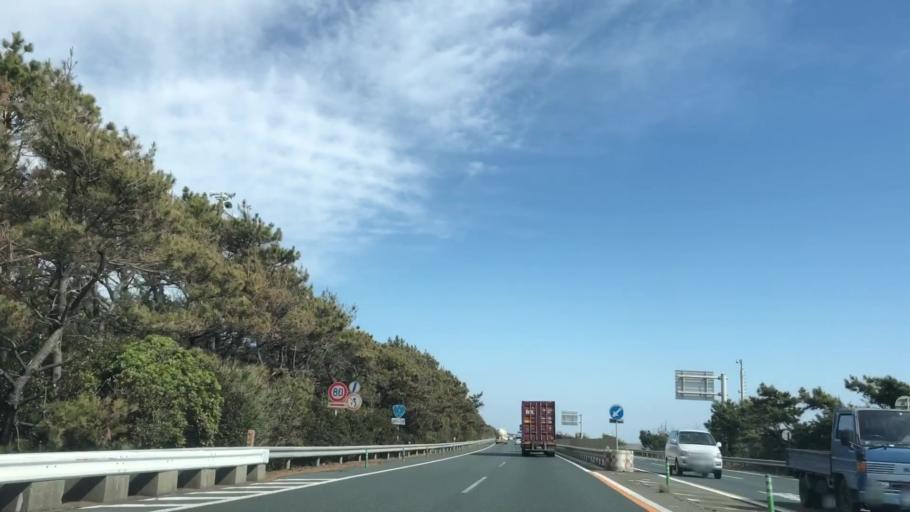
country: JP
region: Shizuoka
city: Kosai-shi
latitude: 34.6794
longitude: 137.5377
